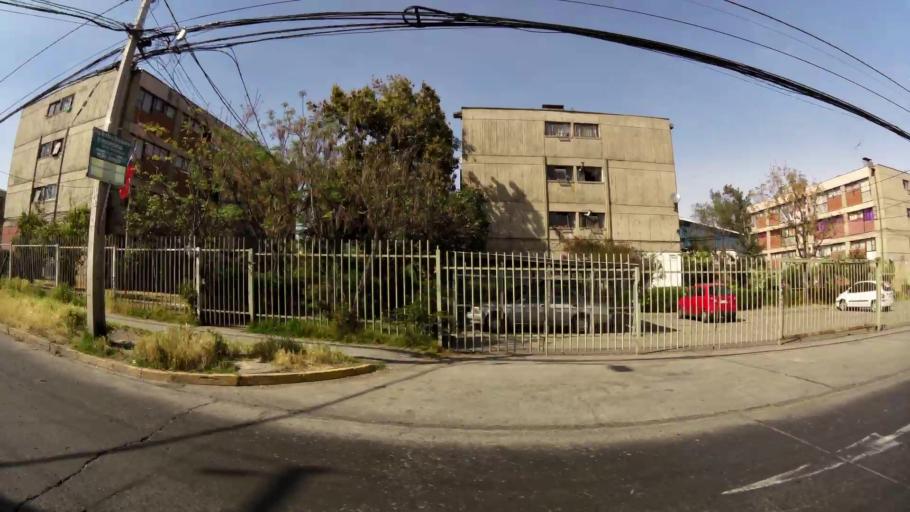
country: CL
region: Santiago Metropolitan
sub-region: Provincia de Cordillera
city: Puente Alto
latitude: -33.6025
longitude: -70.5735
